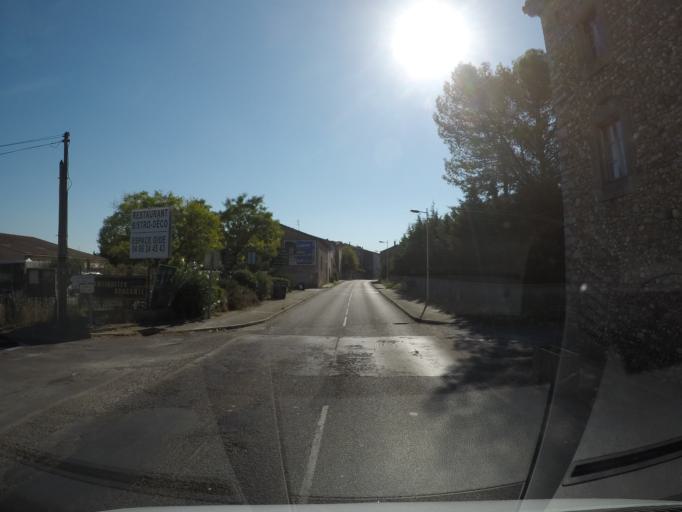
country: FR
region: Languedoc-Roussillon
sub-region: Departement du Gard
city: Boisset-et-Gaujac
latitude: 44.0271
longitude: 4.0211
